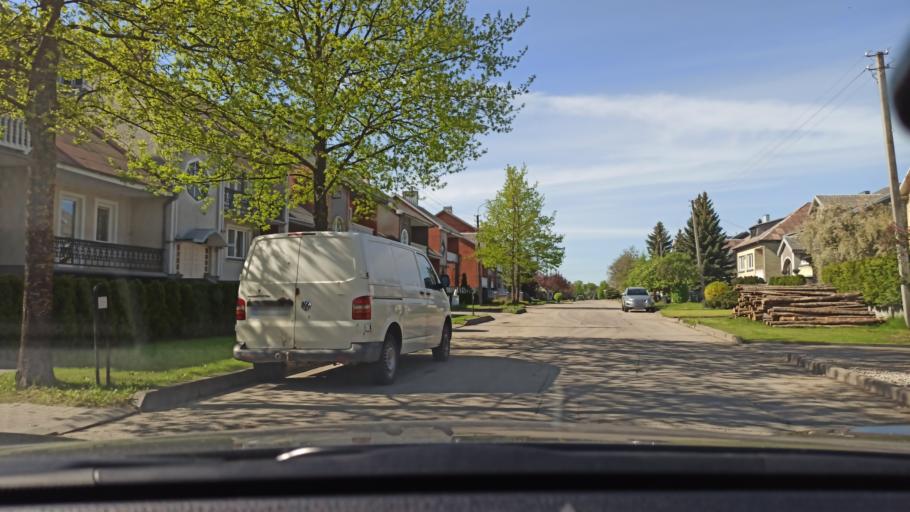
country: LT
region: Siauliu apskritis
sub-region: Siauliai
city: Siauliai
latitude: 55.9567
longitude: 23.2889
